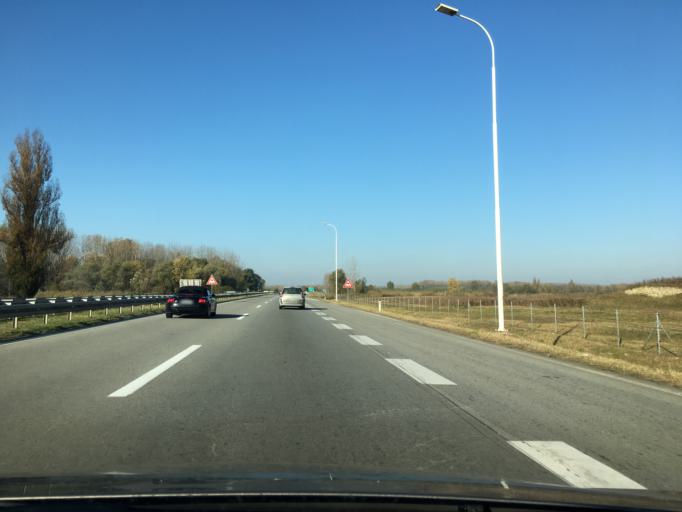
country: RS
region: Autonomna Pokrajina Vojvodina
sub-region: Juznobacki Okrug
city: Petrovaradin
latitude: 45.2768
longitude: 19.9197
